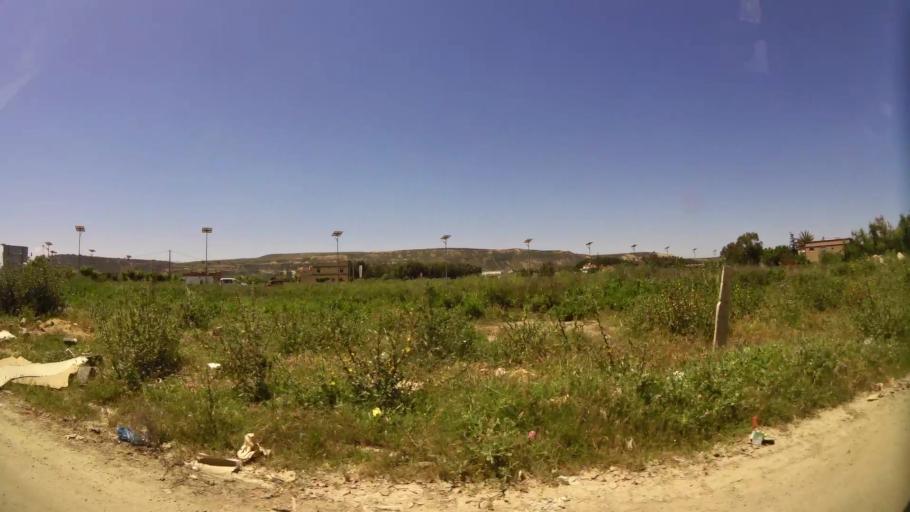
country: MA
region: Oriental
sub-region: Berkane-Taourirt
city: Madagh
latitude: 35.0826
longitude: -2.2441
